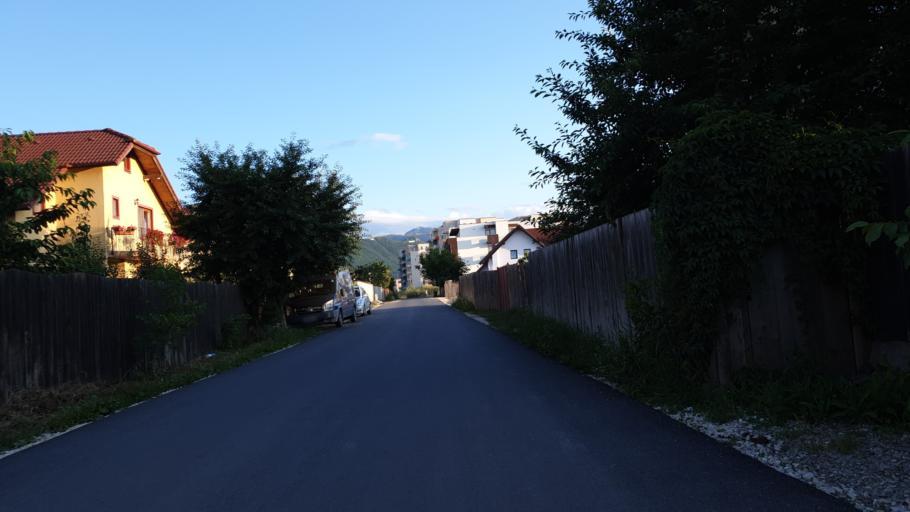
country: RO
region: Brasov
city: Brasov
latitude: 45.6762
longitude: 25.6083
